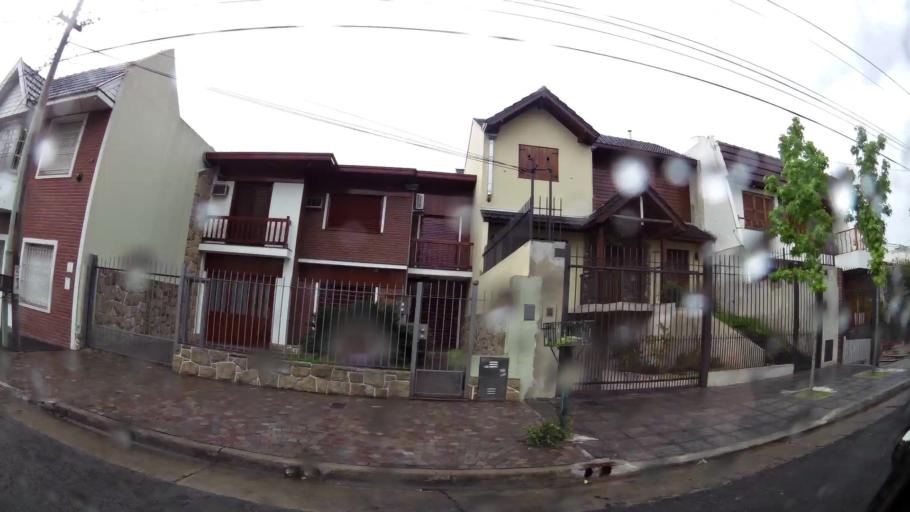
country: AR
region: Buenos Aires
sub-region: Partido de Quilmes
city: Quilmes
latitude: -34.7654
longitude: -58.2192
